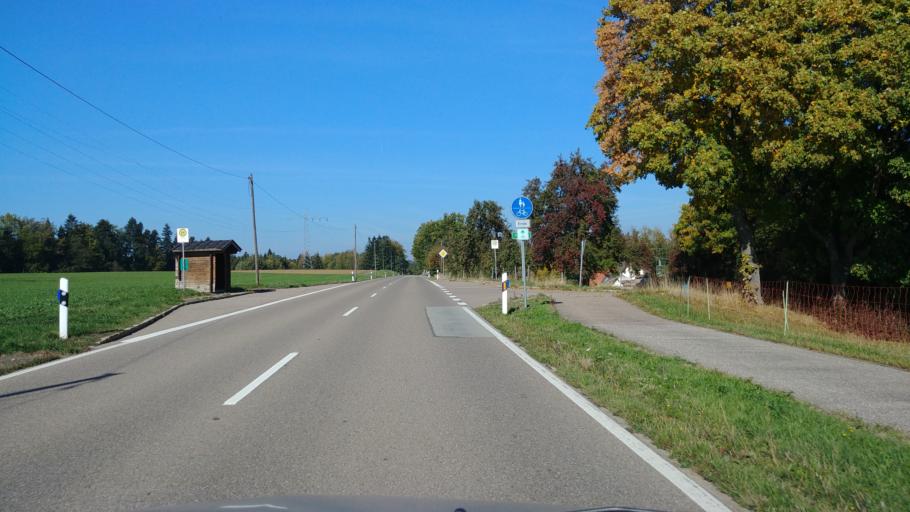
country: DE
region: Baden-Wuerttemberg
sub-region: Regierungsbezirk Stuttgart
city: Spraitbach
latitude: 48.9056
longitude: 9.7495
